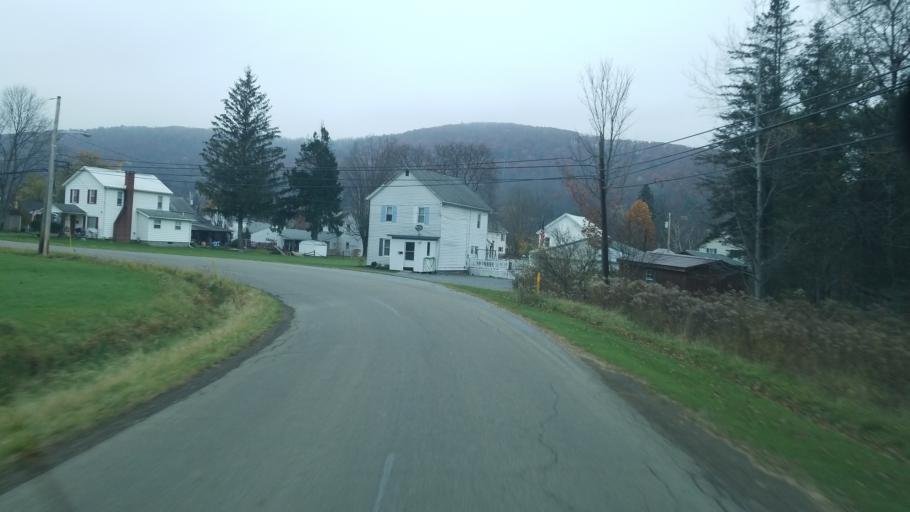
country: US
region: Pennsylvania
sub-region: McKean County
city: Smethport
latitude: 41.8059
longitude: -78.4337
